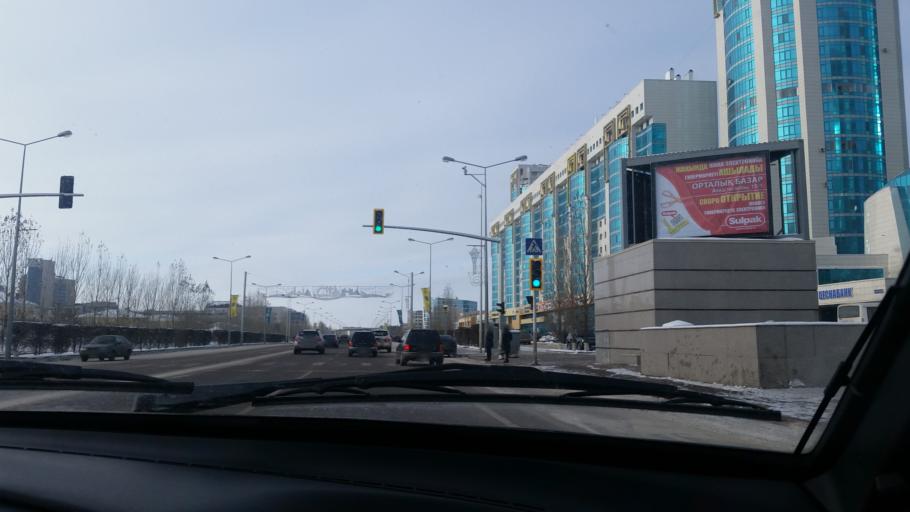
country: KZ
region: Astana Qalasy
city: Astana
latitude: 51.1349
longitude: 71.4256
